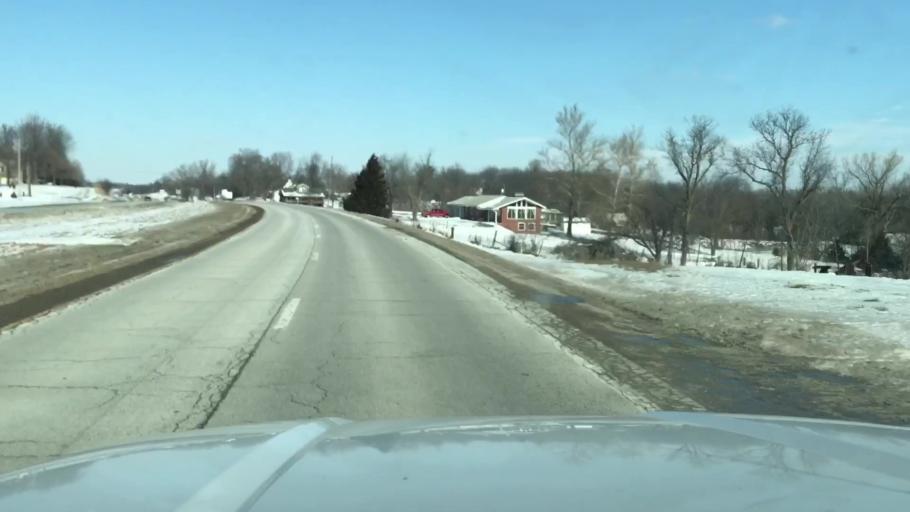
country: US
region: Missouri
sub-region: Andrew County
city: Savannah
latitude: 39.9105
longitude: -94.8092
